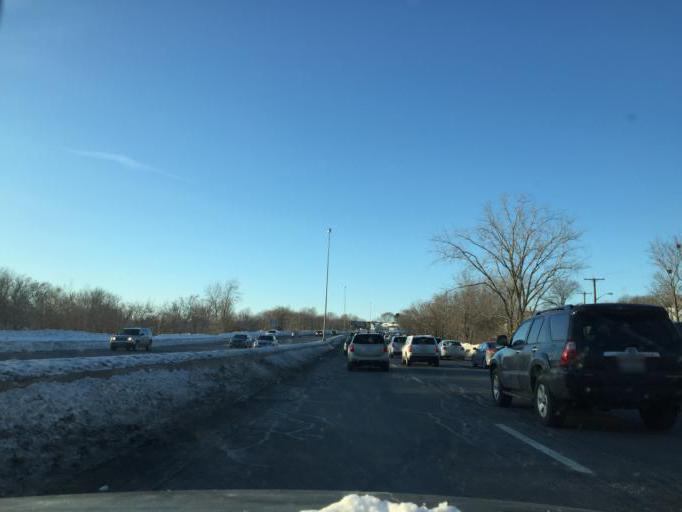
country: US
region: Massachusetts
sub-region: Suffolk County
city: Revere
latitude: 42.4097
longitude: -71.0275
